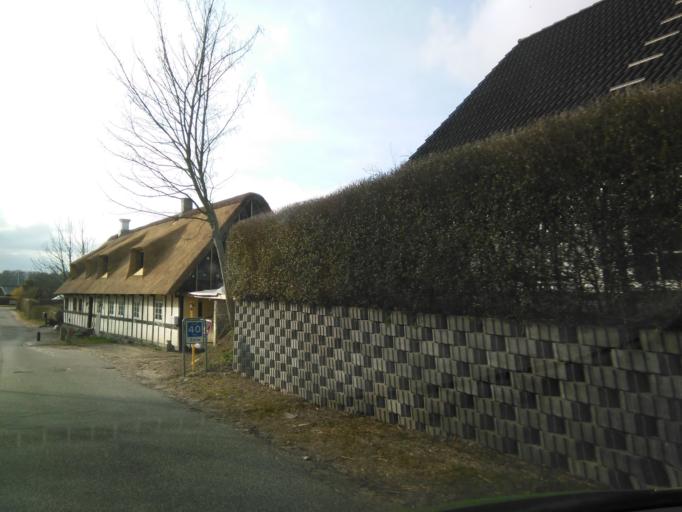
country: DK
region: Central Jutland
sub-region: Arhus Kommune
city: Framlev
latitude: 56.1691
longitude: 10.0438
